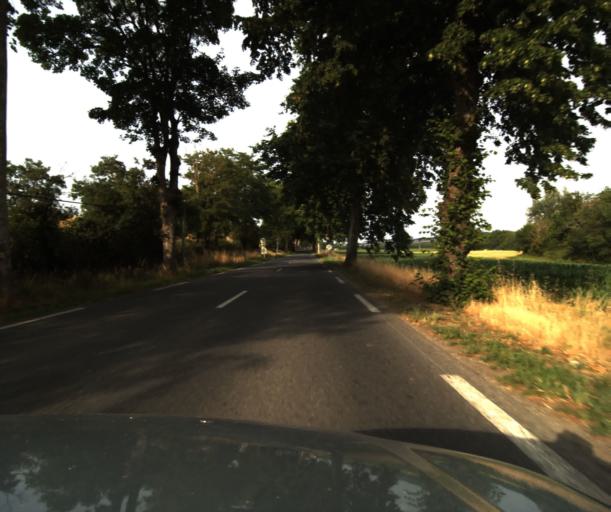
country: FR
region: Midi-Pyrenees
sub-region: Departement du Tarn-et-Garonne
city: Beaumont-de-Lomagne
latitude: 43.8927
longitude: 1.0145
